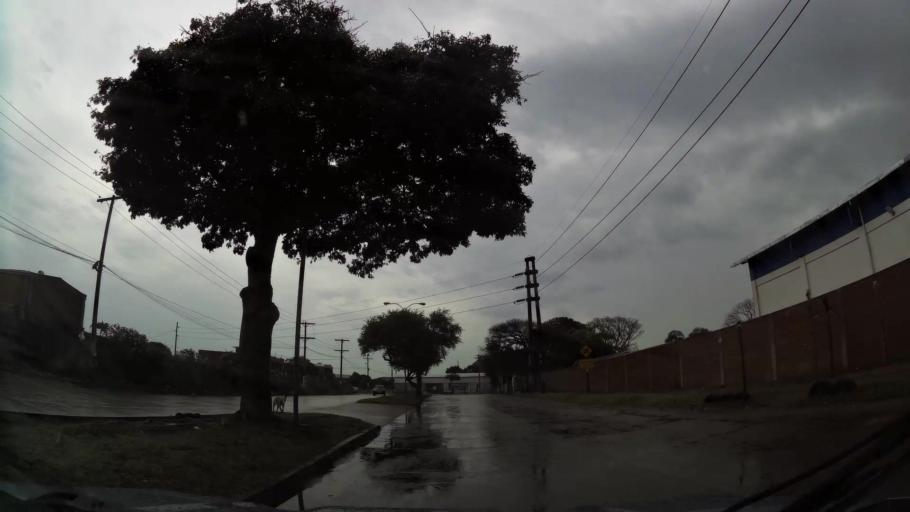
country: BO
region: Santa Cruz
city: Santa Cruz de la Sierra
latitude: -17.7910
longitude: -63.1552
